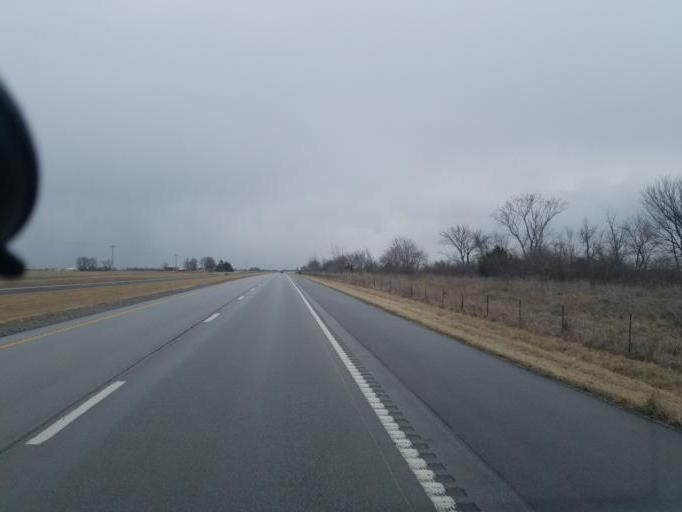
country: US
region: Missouri
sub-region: Macon County
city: Macon
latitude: 39.8365
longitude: -92.4776
